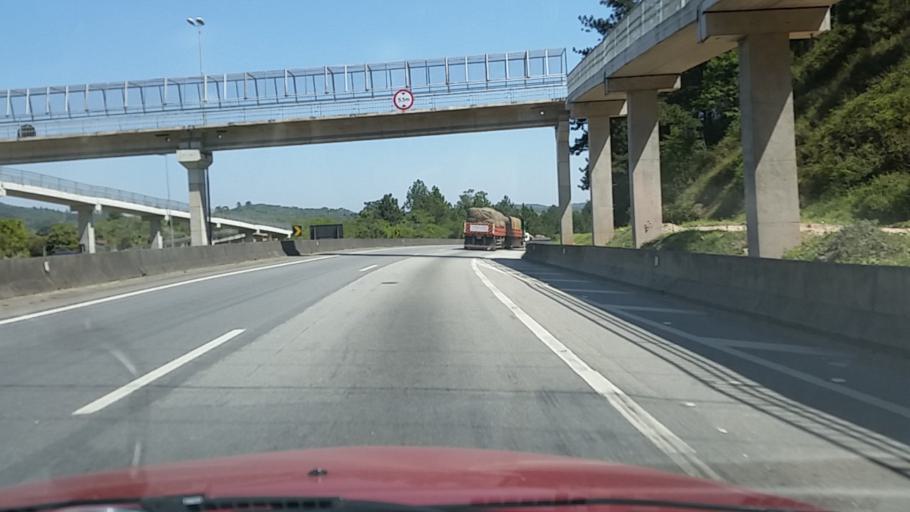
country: BR
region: Sao Paulo
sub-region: Juquitiba
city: Juquitiba
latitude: -23.9374
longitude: -47.0821
